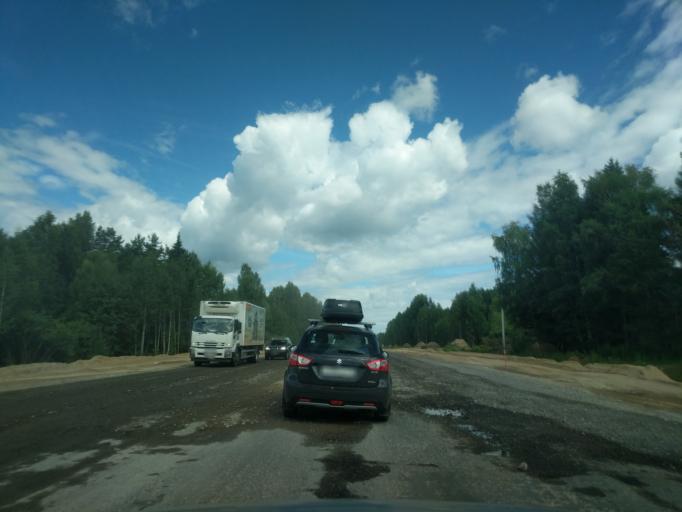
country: RU
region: Jaroslavl
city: Levashevo
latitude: 57.6584
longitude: 40.5659
